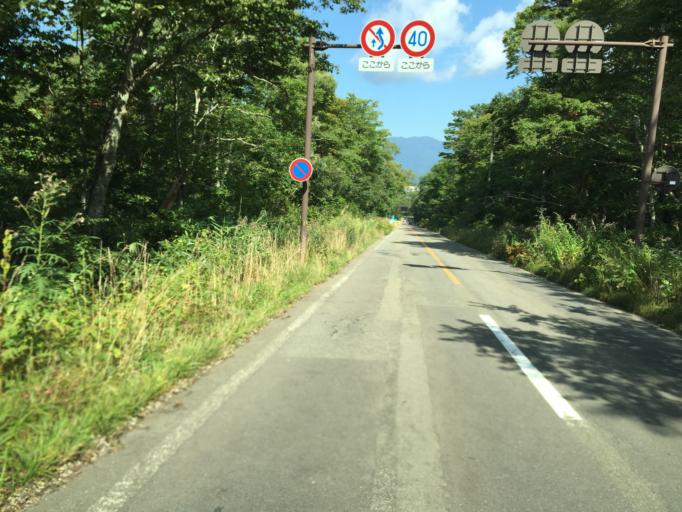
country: JP
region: Fukushima
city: Inawashiro
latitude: 37.6448
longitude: 140.0516
